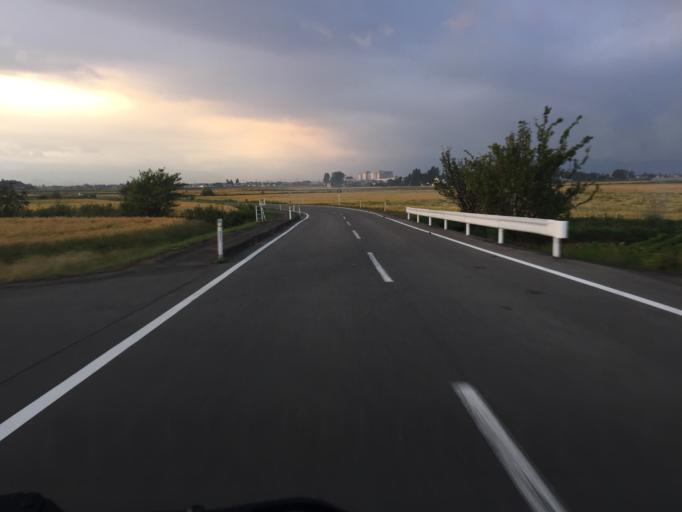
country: JP
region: Fukushima
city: Kitakata
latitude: 37.5624
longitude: 139.9167
